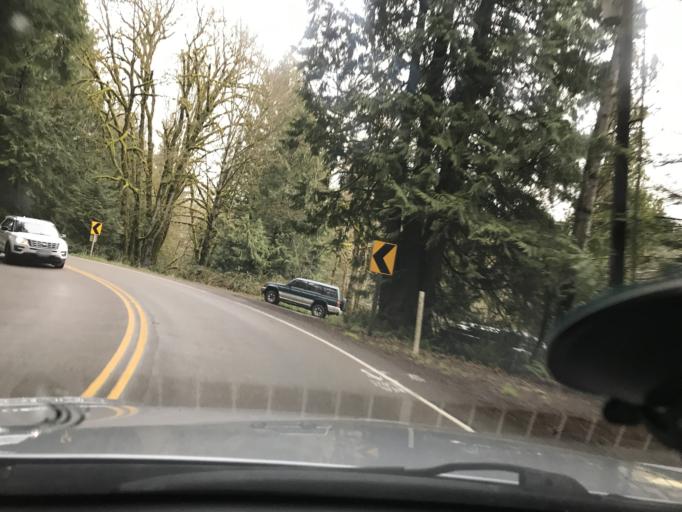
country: US
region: Washington
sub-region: King County
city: Ames Lake
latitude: 47.6455
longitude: -121.9587
